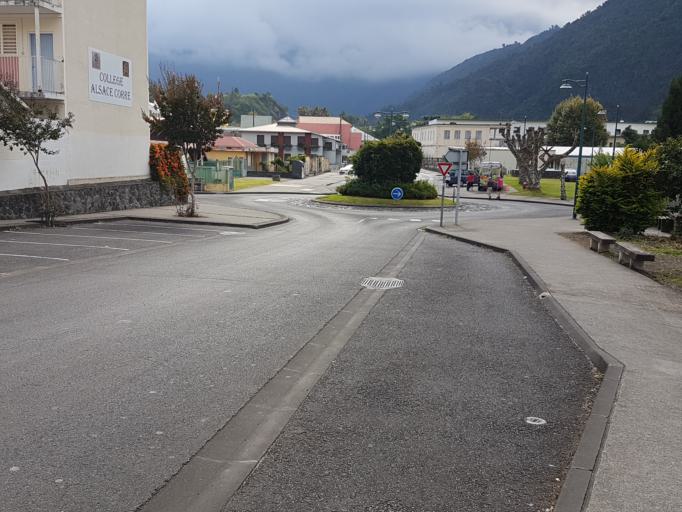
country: RE
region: Reunion
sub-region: Reunion
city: Cilaos
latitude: -21.1341
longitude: 55.4736
